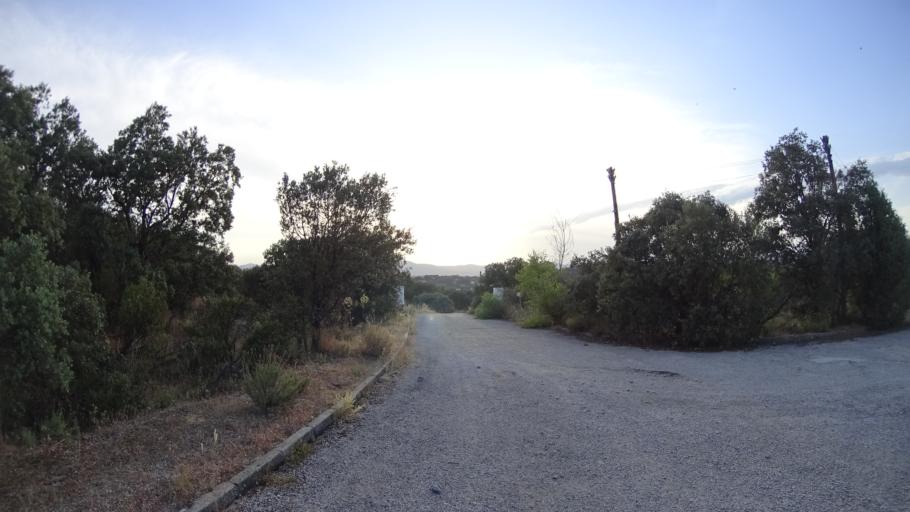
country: ES
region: Madrid
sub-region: Provincia de Madrid
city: Torrelodones
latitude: 40.5924
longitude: -3.9457
